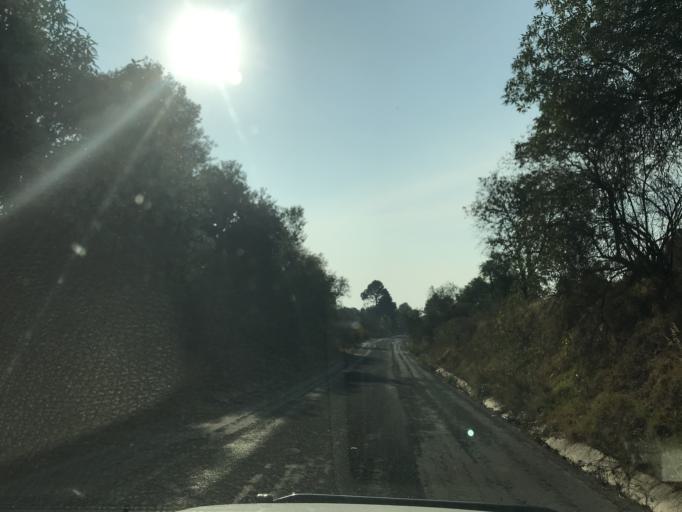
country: MX
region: Puebla
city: San Nicolas de los Ranchos
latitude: 19.0867
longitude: -98.5295
